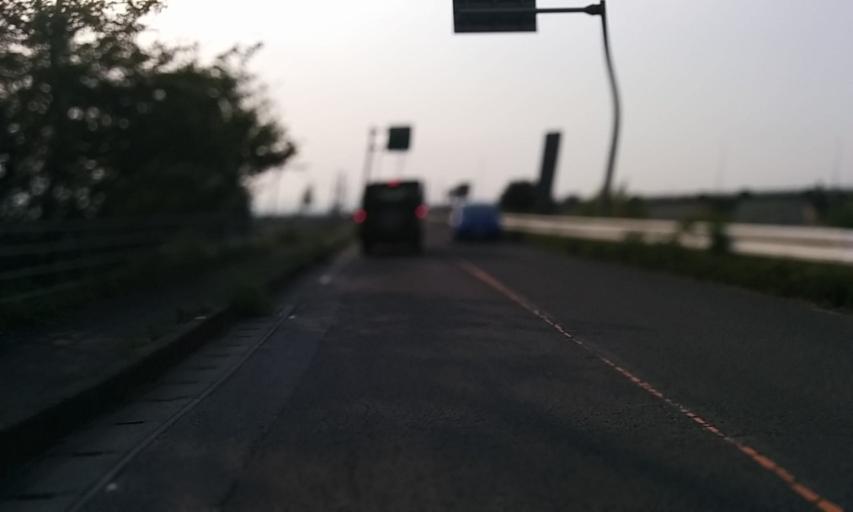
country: JP
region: Ehime
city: Saijo
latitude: 33.9014
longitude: 133.1852
